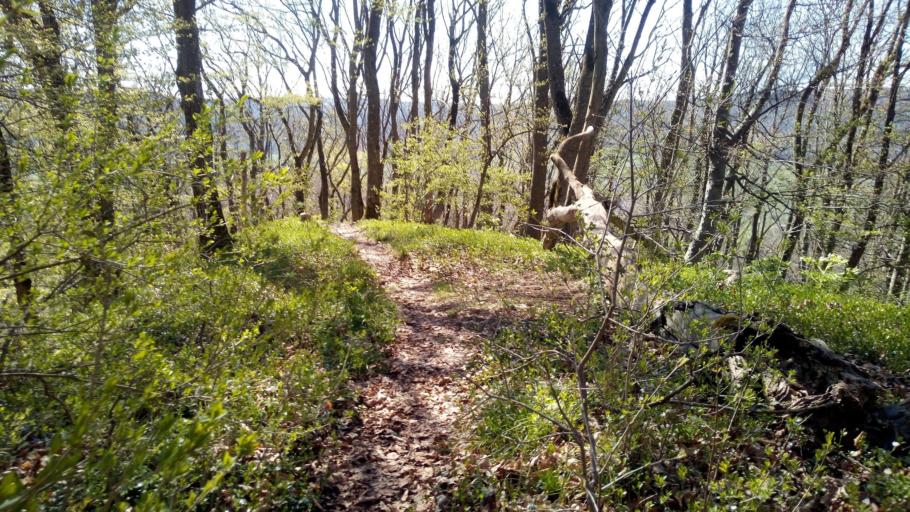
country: DE
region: Baden-Wuerttemberg
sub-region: Regierungsbezirk Stuttgart
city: Donzdorf
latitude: 48.7134
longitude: 9.8415
